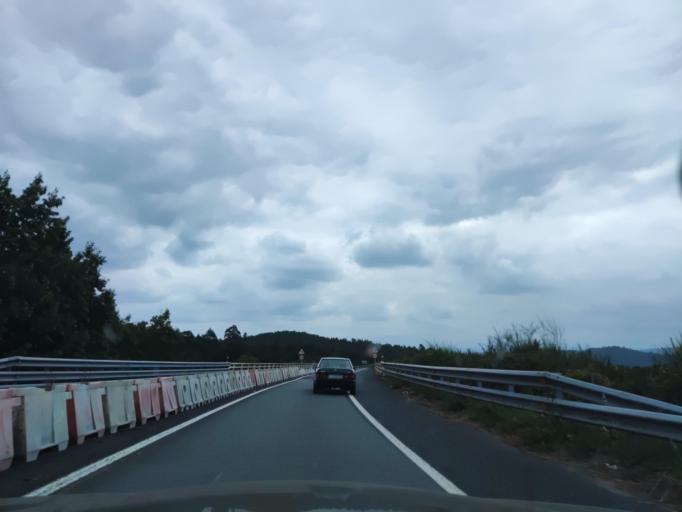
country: ES
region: Galicia
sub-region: Provincia da Coruna
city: Teo
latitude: 42.7875
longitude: -8.5480
